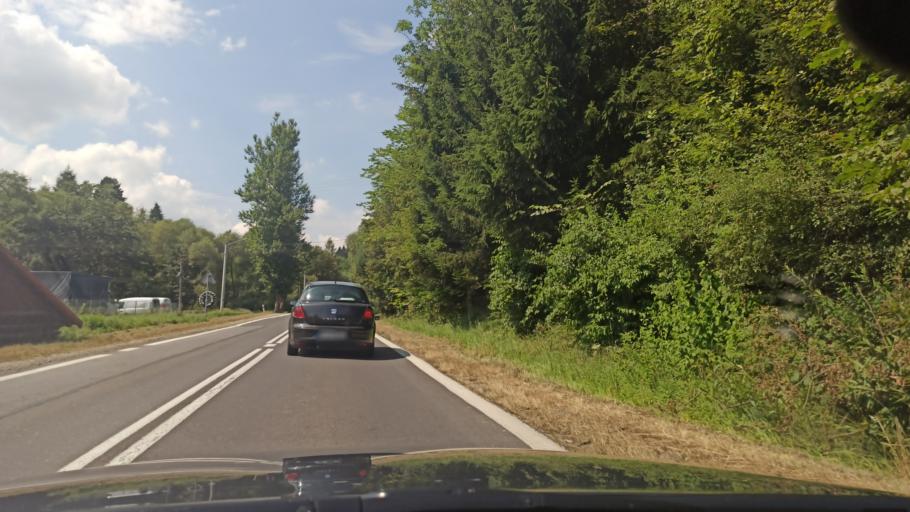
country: PL
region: Lesser Poland Voivodeship
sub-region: Powiat nowotarski
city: Krosnica
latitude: 49.4378
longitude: 20.3620
